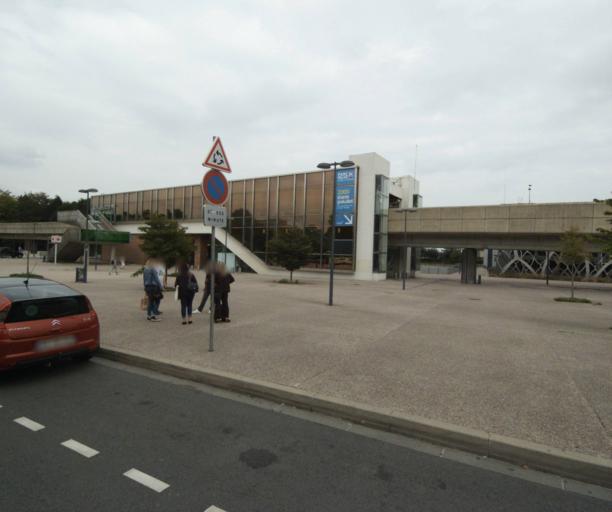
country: FR
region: Nord-Pas-de-Calais
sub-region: Departement du Nord
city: Lezennes
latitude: 50.6050
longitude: 3.1384
